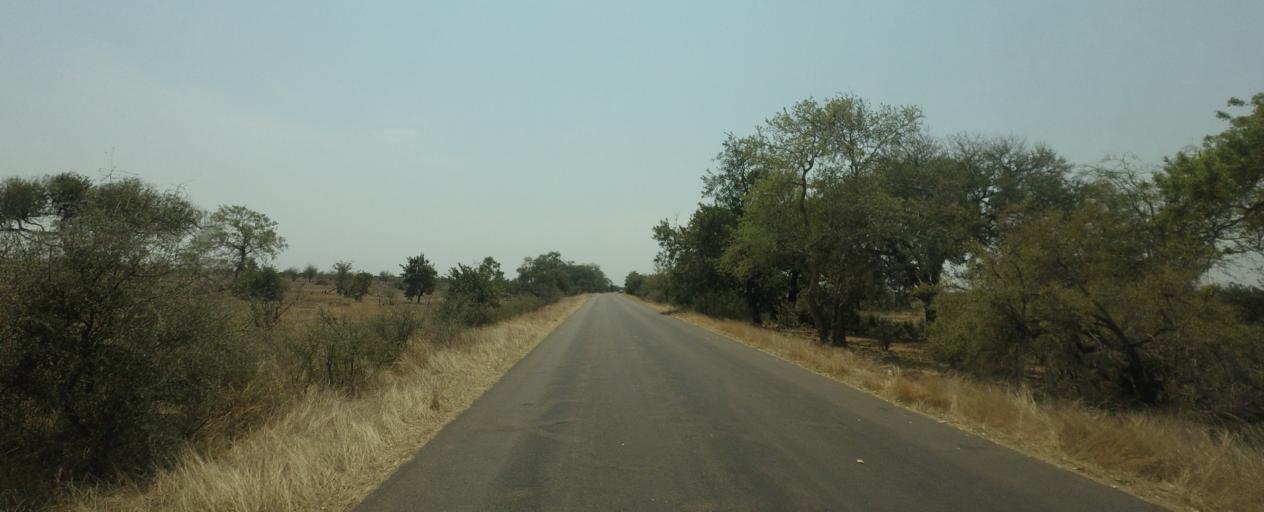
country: ZA
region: Limpopo
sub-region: Mopani District Municipality
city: Phalaborwa
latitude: -24.1626
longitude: 31.7201
